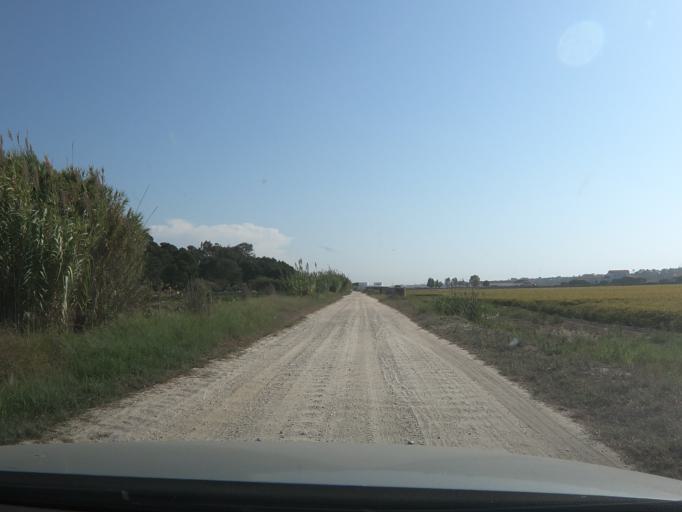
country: PT
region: Setubal
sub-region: Setubal
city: Setubal
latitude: 38.3867
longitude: -8.7894
